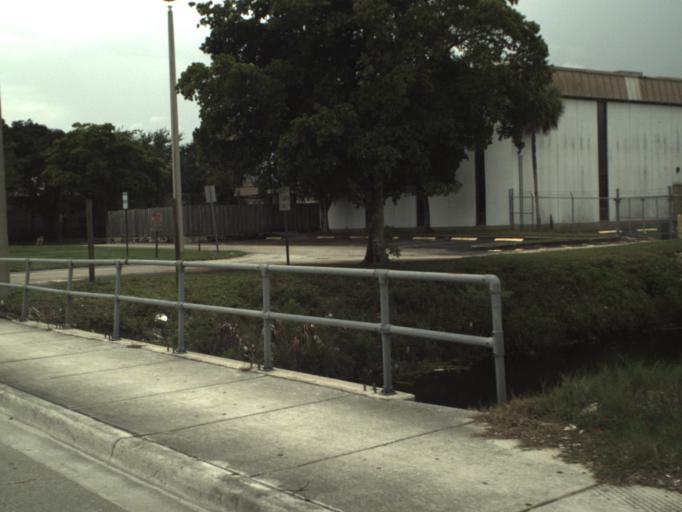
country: US
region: Florida
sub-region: Palm Beach County
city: Palm Springs
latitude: 26.6480
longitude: -80.1125
